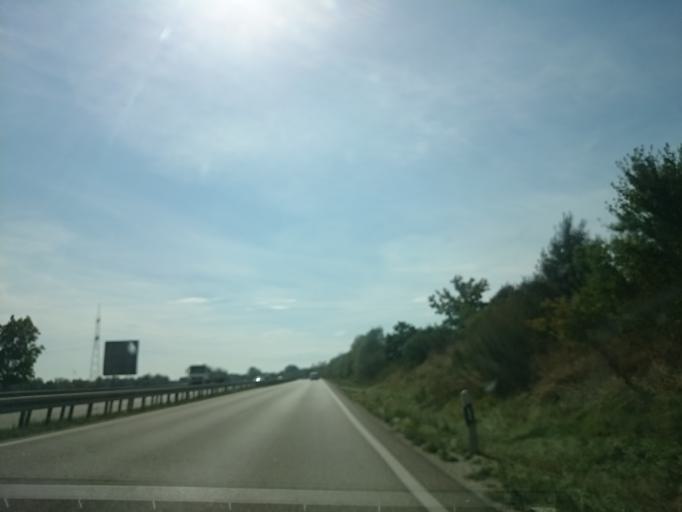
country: DE
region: Bavaria
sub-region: Swabia
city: Langweid
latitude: 48.5148
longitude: 10.8408
